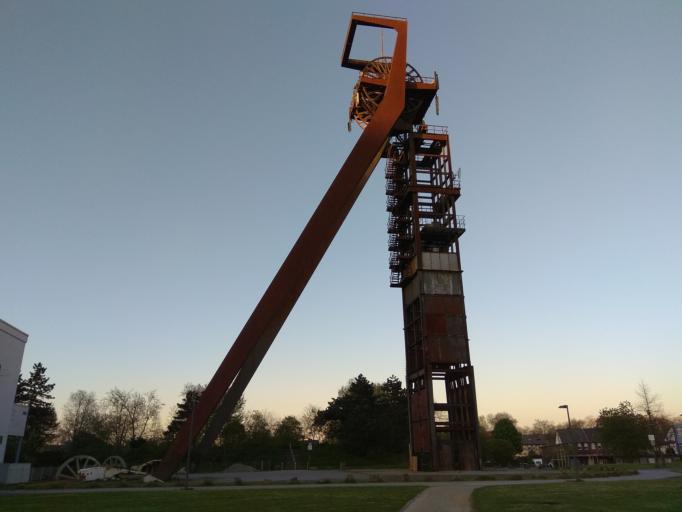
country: DE
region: North Rhine-Westphalia
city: Herten
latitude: 51.5644
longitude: 7.1787
